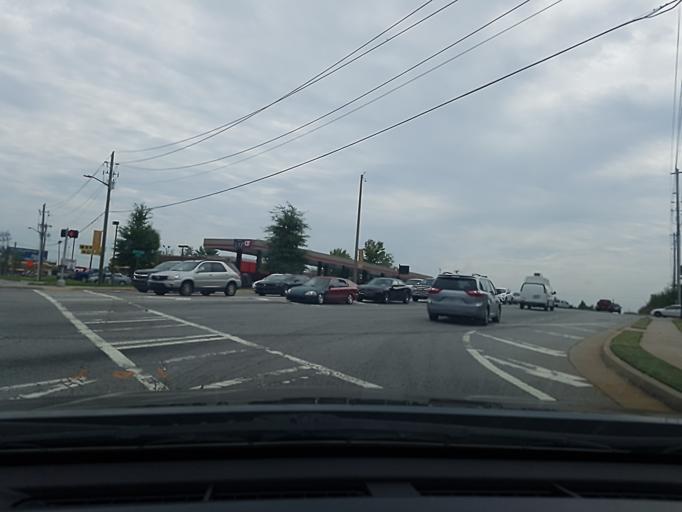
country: US
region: Georgia
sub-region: Gwinnett County
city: Duluth
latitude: 33.9548
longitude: -84.1415
